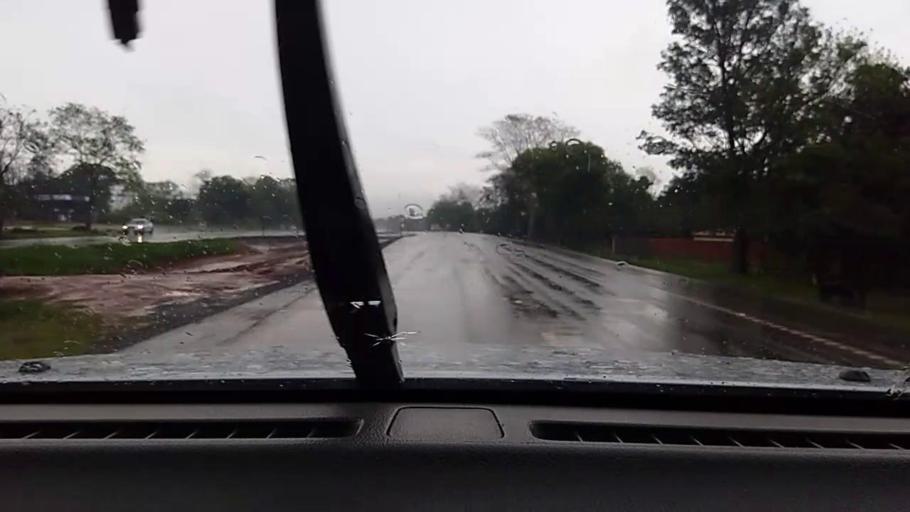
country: PY
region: Caaguazu
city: Repatriacion
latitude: -25.4539
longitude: -55.9091
